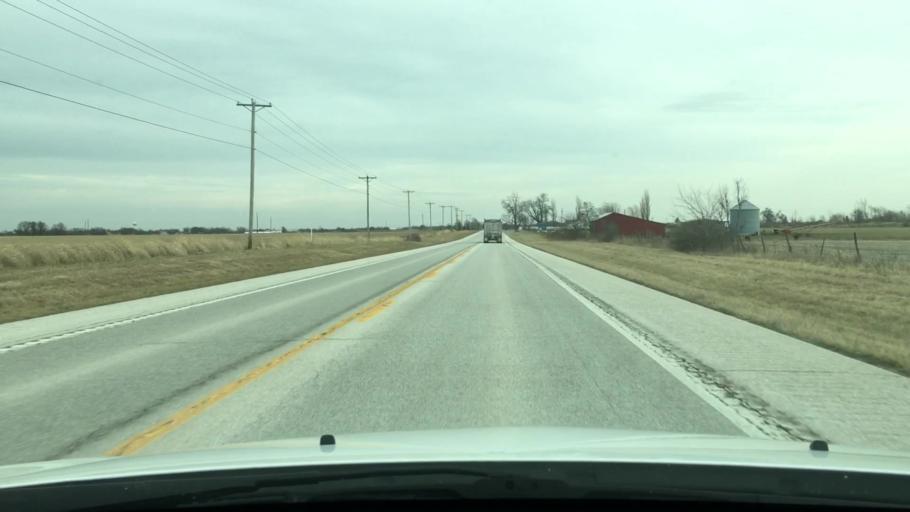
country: US
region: Missouri
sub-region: Pike County
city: Bowling Green
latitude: 39.3443
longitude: -91.2605
